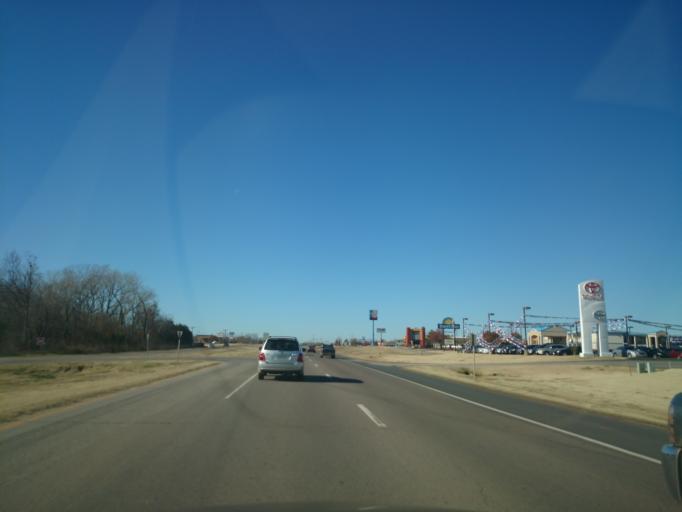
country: US
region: Oklahoma
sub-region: Payne County
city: Stillwater
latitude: 36.1160
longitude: -97.1248
